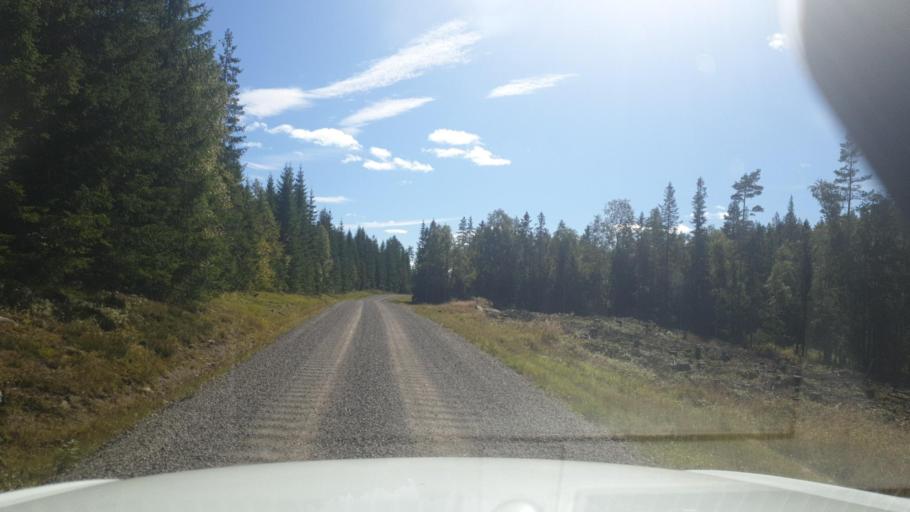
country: SE
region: Vaermland
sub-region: Eda Kommun
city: Charlottenberg
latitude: 60.0777
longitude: 12.6200
